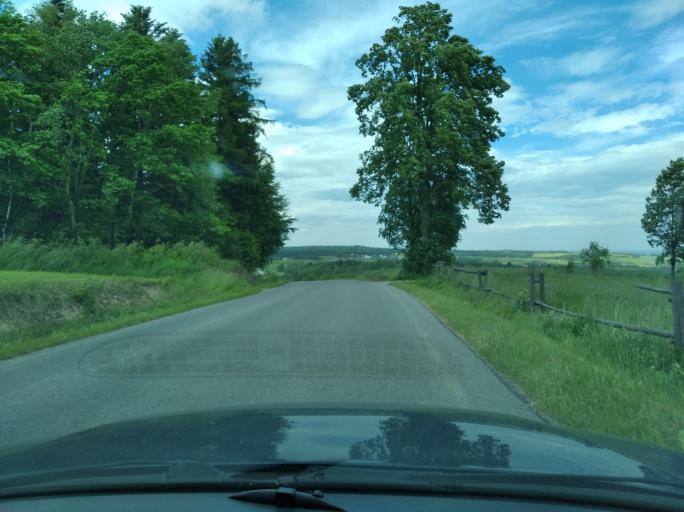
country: PL
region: Subcarpathian Voivodeship
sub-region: Powiat ropczycko-sedziszowski
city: Wielopole Skrzynskie
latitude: 49.9857
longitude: 21.6170
